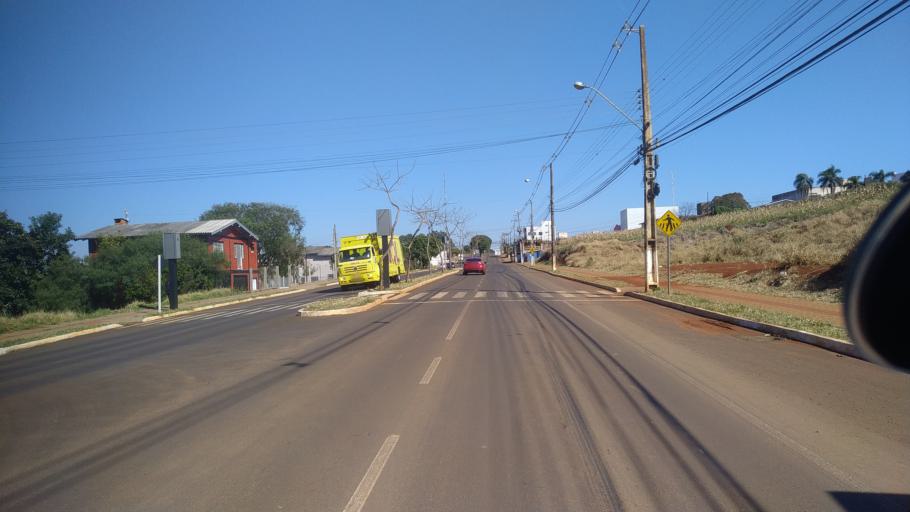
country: BR
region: Santa Catarina
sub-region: Chapeco
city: Chapeco
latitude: -27.0897
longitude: -52.5918
